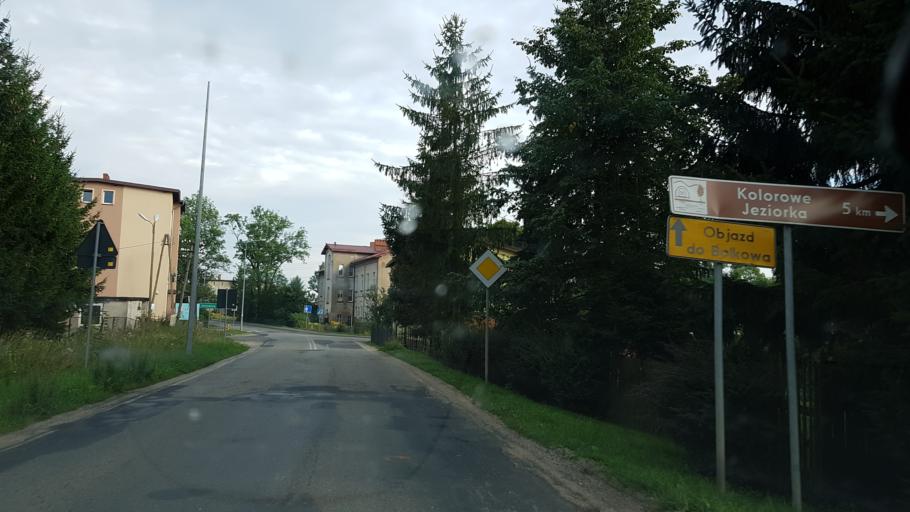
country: PL
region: Lower Silesian Voivodeship
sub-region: Powiat kamiennogorski
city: Marciszow
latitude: 50.8546
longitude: 16.0026
